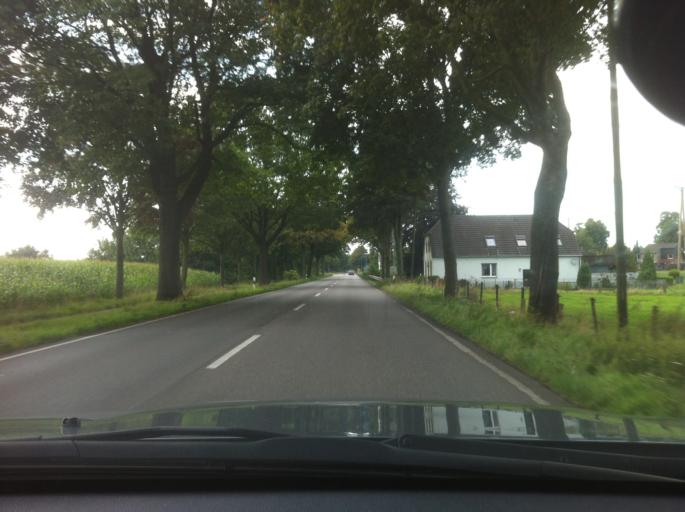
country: DE
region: North Rhine-Westphalia
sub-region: Regierungsbezirk Dusseldorf
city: Kleve
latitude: 51.7569
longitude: 6.1528
